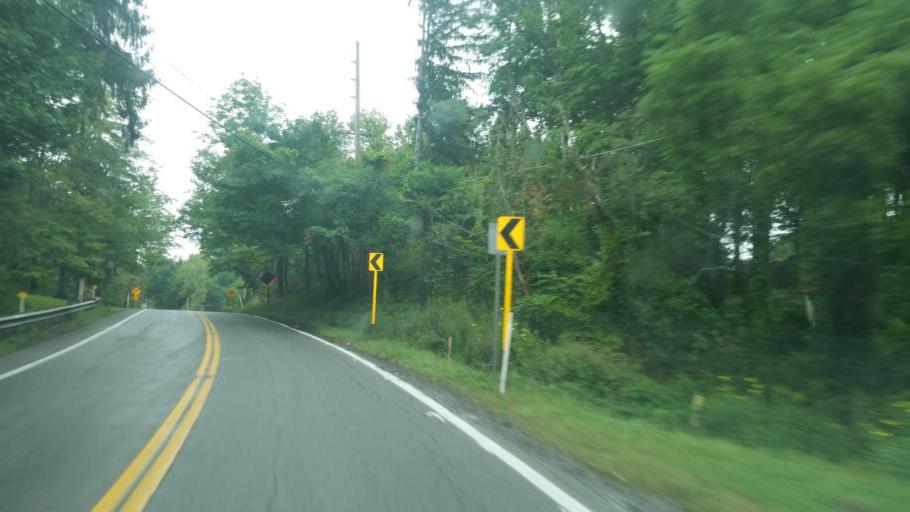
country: US
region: Ohio
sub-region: Geauga County
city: Burton
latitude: 41.4446
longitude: -81.2070
